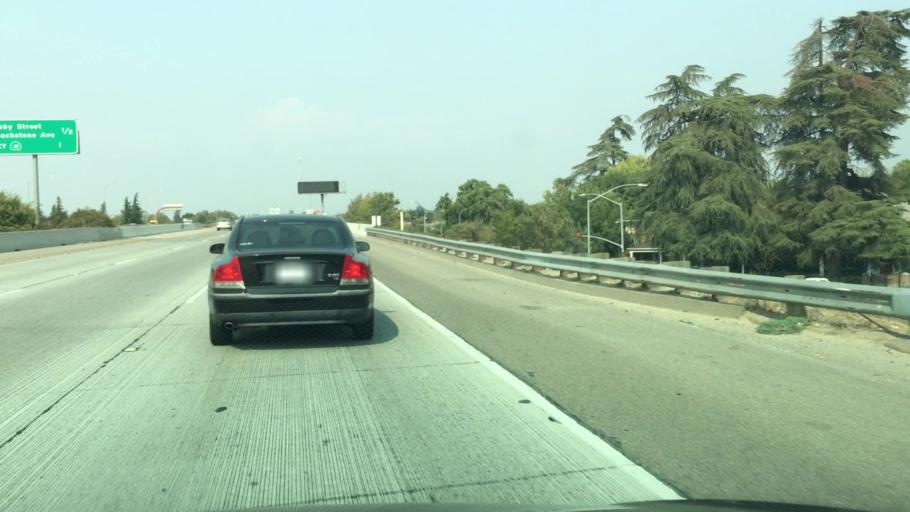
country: US
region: California
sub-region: Fresno County
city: Fresno
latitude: 36.7480
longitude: -119.8010
